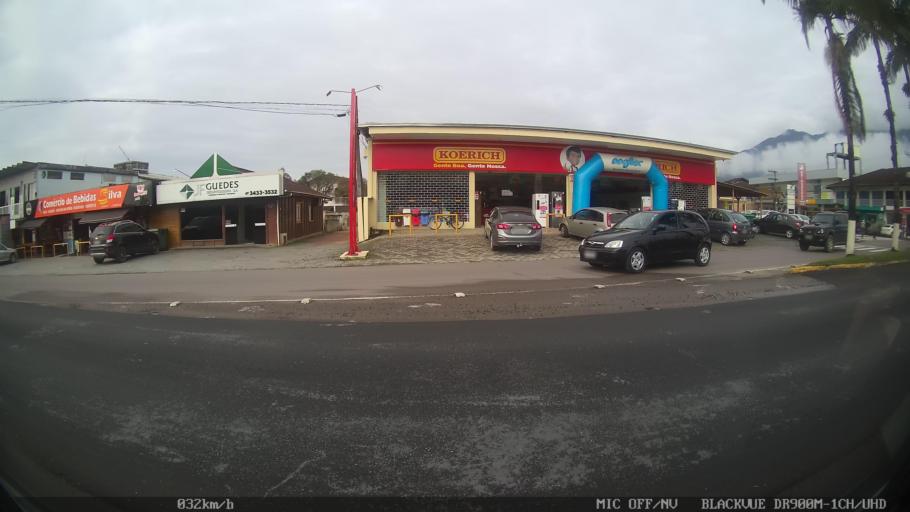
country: BR
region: Santa Catarina
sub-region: Joinville
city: Joinville
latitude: -26.0299
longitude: -48.8549
